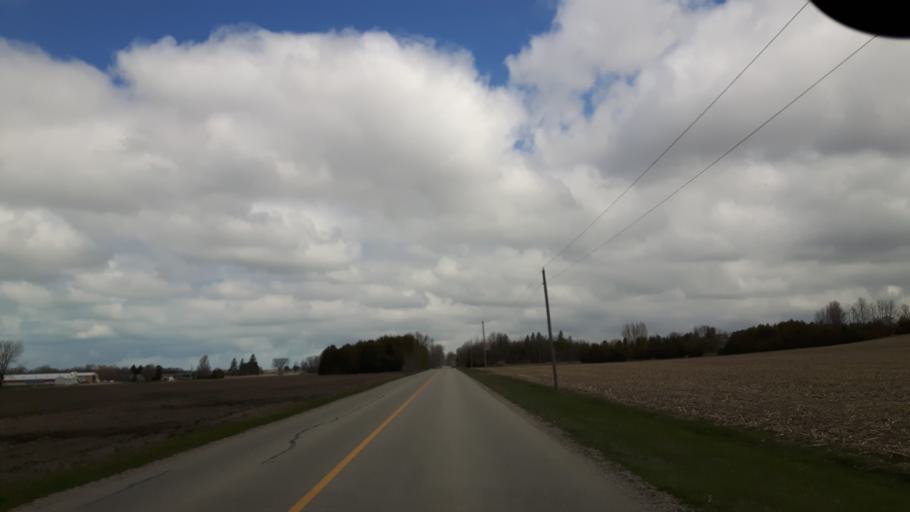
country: CA
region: Ontario
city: Goderich
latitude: 43.6811
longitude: -81.6847
